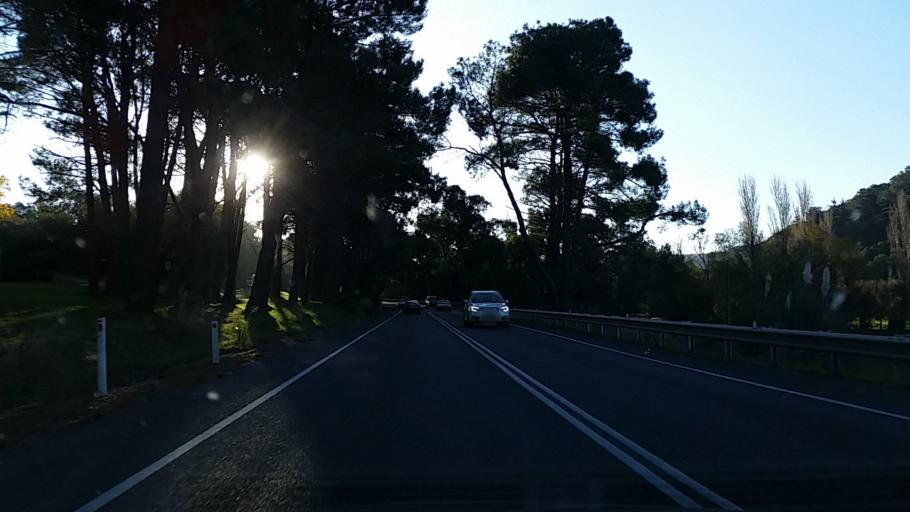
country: AU
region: South Australia
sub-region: Alexandrina
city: Mount Compass
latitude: -35.3453
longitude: 138.6161
